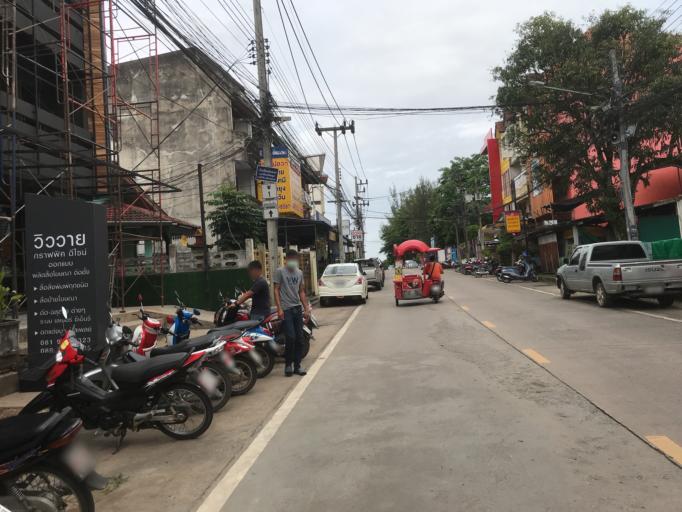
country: TH
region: Chiang Rai
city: Chiang Rai
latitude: 19.9025
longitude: 99.8160
